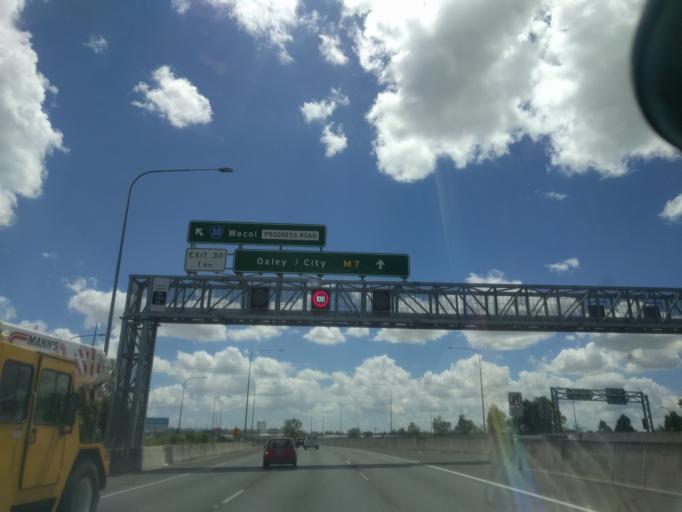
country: AU
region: Queensland
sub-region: Brisbane
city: Wacol
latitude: -27.6048
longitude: 152.9174
